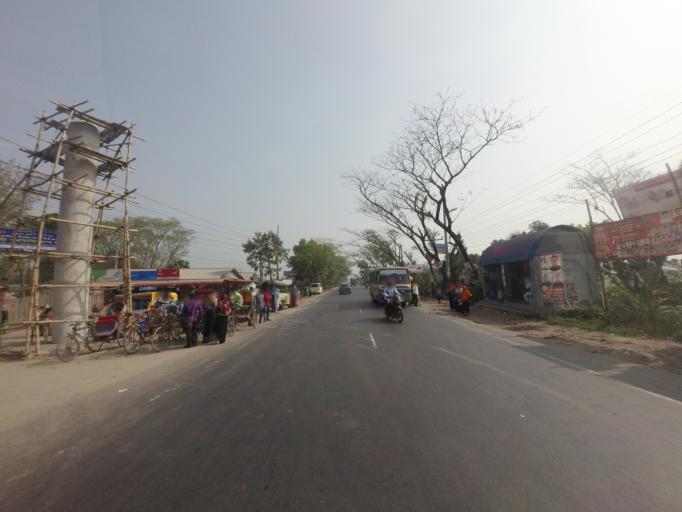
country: BD
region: Dhaka
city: Narsingdi
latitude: 23.8406
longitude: 90.6207
